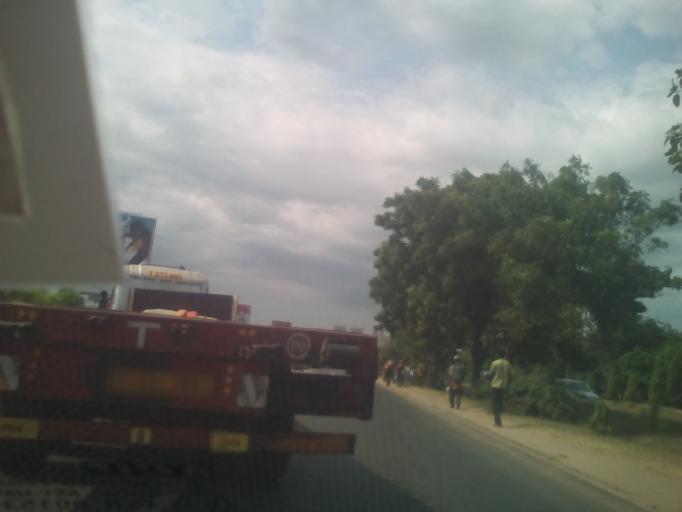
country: TZ
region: Dar es Salaam
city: Dar es Salaam
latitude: -6.8335
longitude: 39.2666
